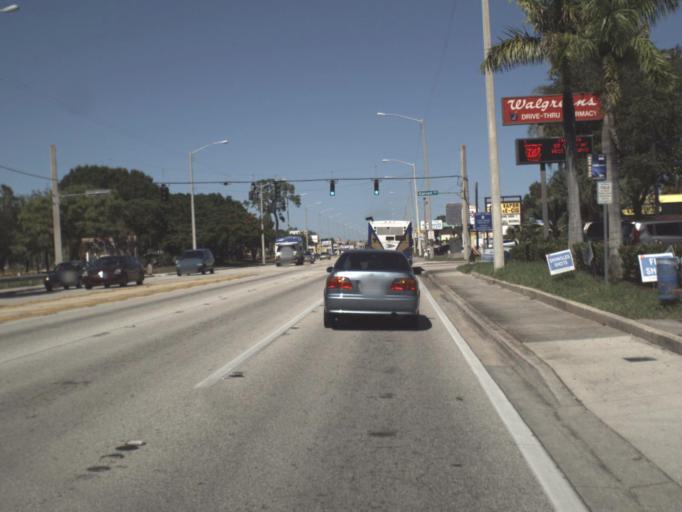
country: US
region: Florida
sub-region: Lee County
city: Fort Myers
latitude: 26.6110
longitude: -81.8719
